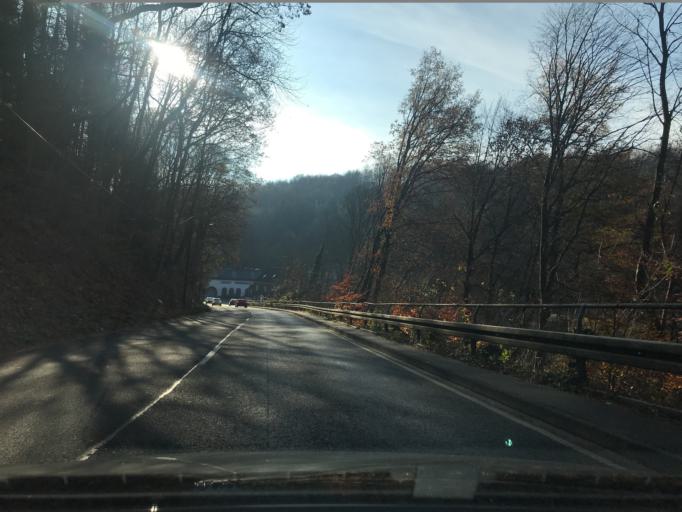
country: DE
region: North Rhine-Westphalia
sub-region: Regierungsbezirk Dusseldorf
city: Remscheid
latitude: 51.1714
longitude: 7.1559
